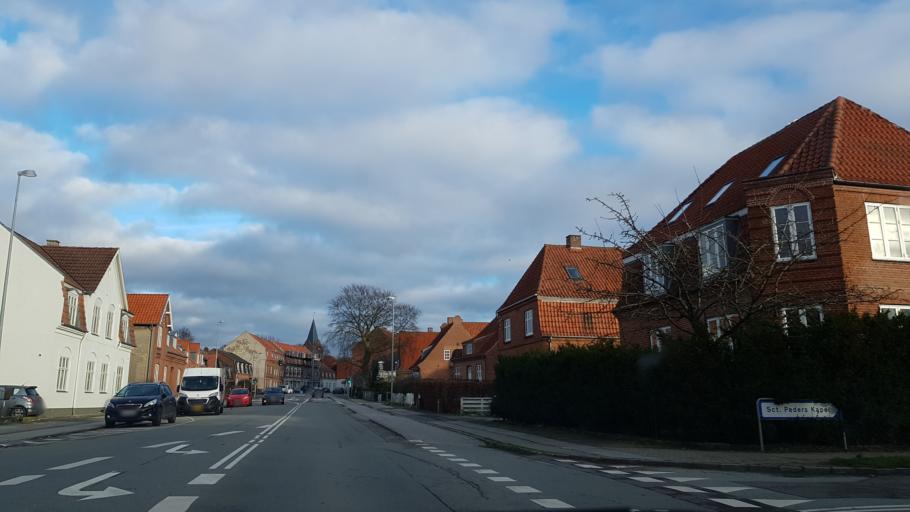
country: DK
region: Zealand
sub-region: Slagelse Kommune
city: Slagelse
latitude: 55.3996
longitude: 11.3450
